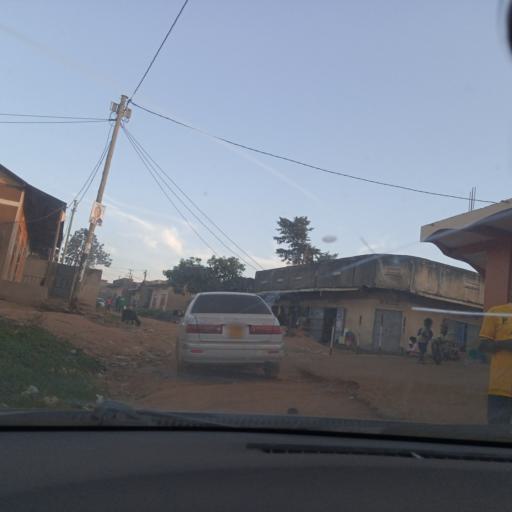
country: UG
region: Central Region
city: Masaka
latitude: -0.3217
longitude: 31.7587
